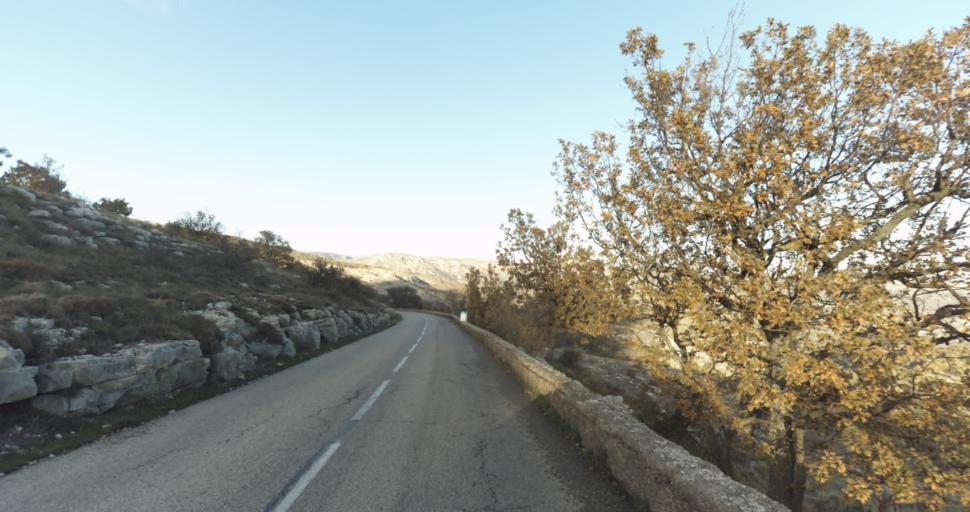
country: FR
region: Provence-Alpes-Cote d'Azur
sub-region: Departement des Alpes-Maritimes
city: Vence
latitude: 43.7584
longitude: 7.0815
